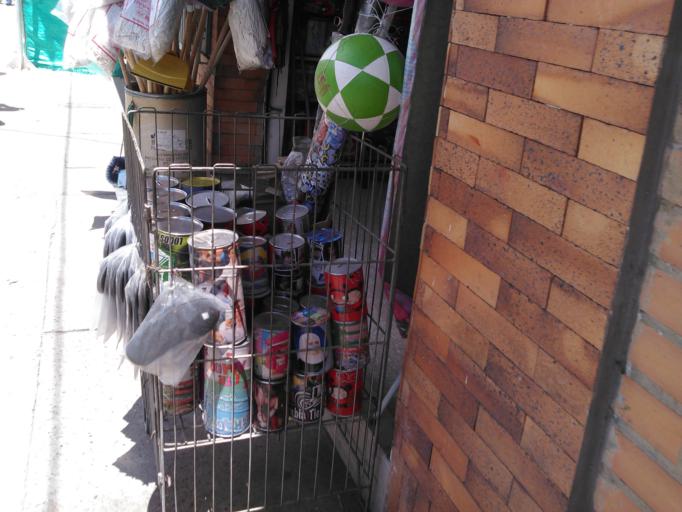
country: CO
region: Bogota D.C.
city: Bogota
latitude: 4.6204
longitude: -74.1218
